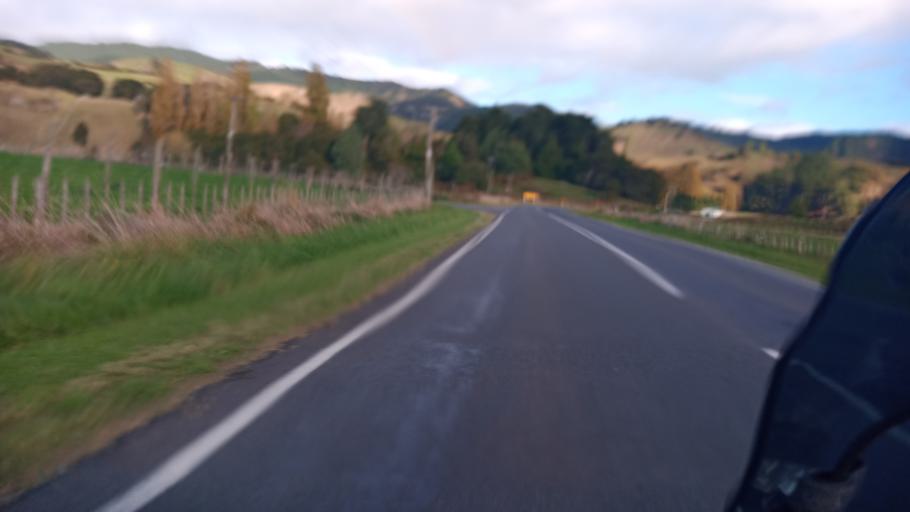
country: NZ
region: Gisborne
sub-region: Gisborne District
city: Gisborne
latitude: -38.6325
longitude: 177.8284
